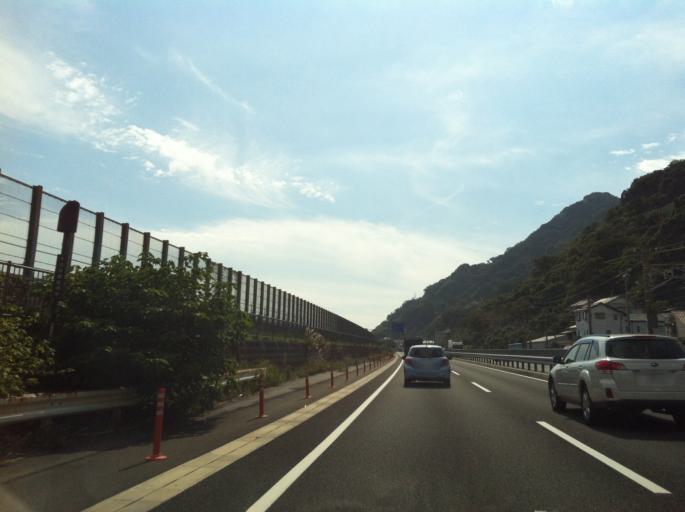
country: JP
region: Shizuoka
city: Fujinomiya
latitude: 35.0902
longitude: 138.5496
